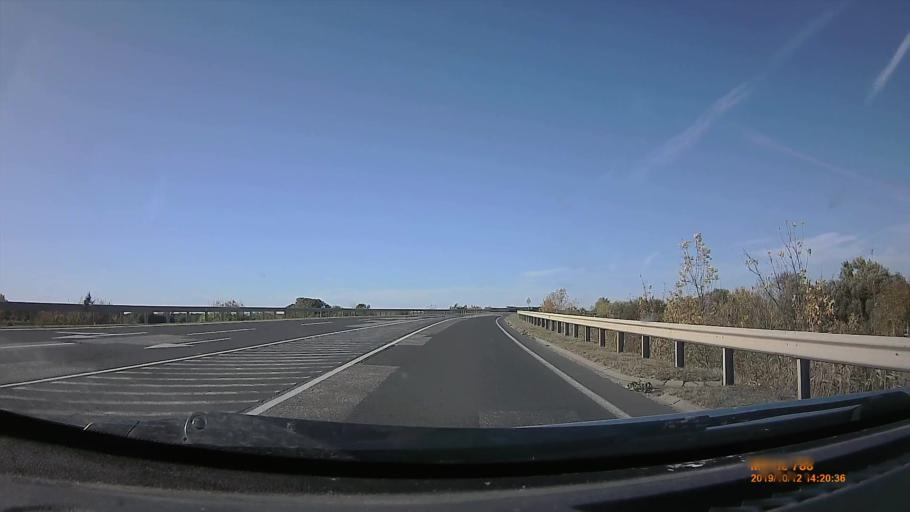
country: HU
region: Hajdu-Bihar
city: Biharkeresztes
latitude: 47.1312
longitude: 21.7446
